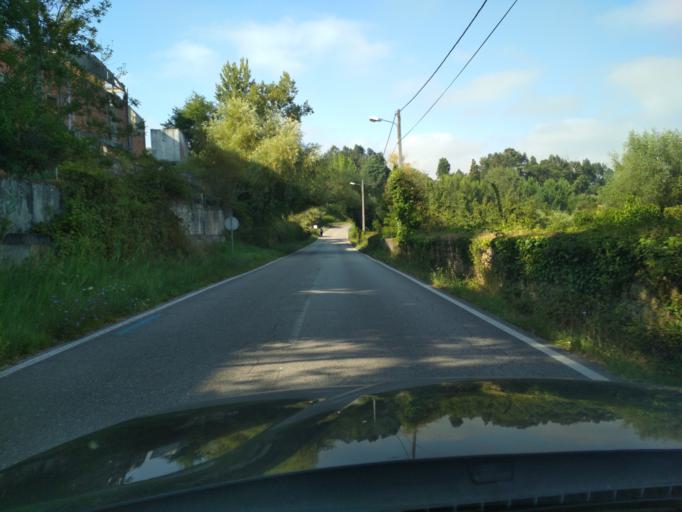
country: PT
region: Coimbra
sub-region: Condeixa-A-Nova
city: Condeixa-a-Nova
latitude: 40.1485
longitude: -8.4661
